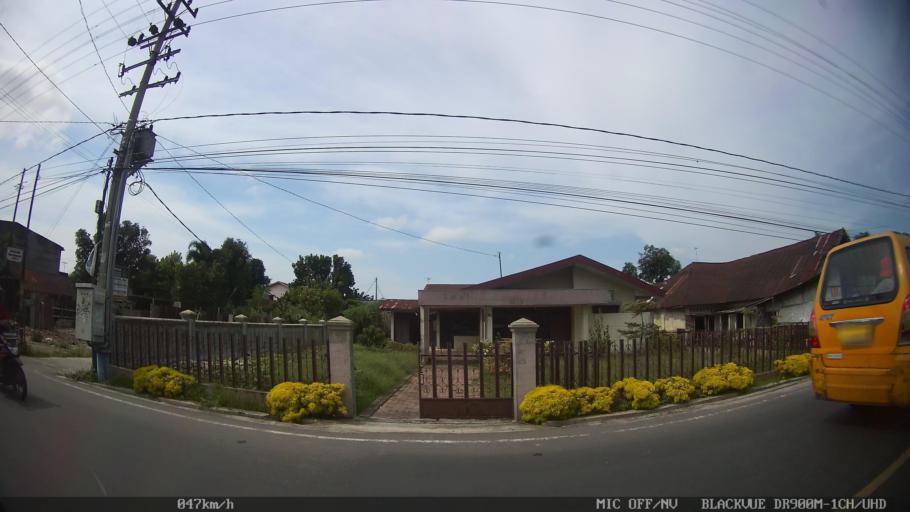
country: ID
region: North Sumatra
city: Percut
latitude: 3.6072
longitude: 98.7716
